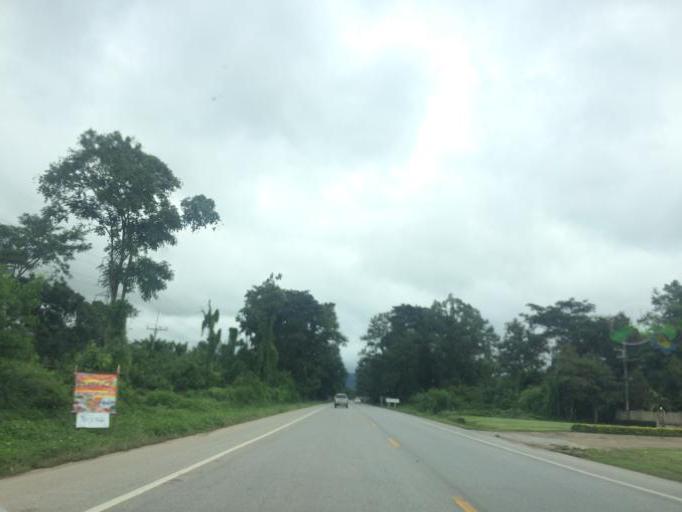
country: TH
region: Chiang Rai
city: Mae Lao
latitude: 19.7463
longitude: 99.7080
